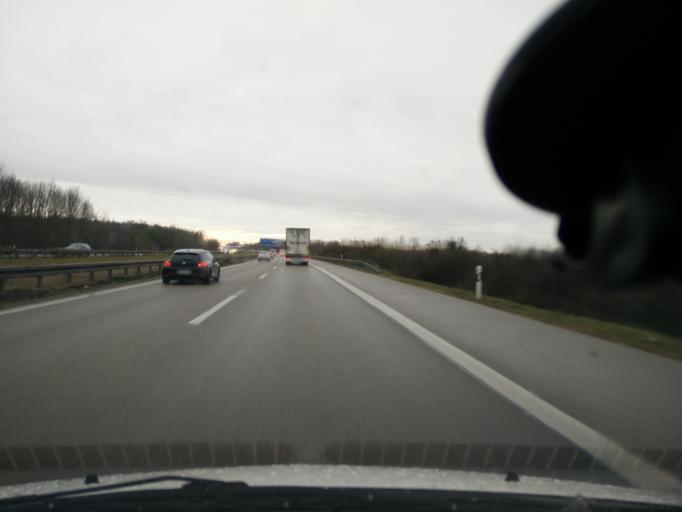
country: DE
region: Bavaria
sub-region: Upper Bavaria
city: Oberschleissheim
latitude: 48.2426
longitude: 11.5346
